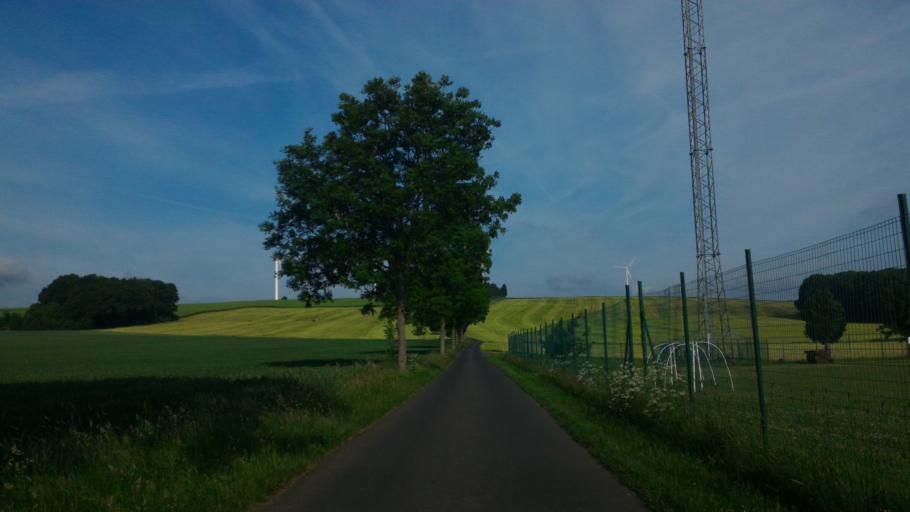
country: DE
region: Saxony
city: Leutersdorf
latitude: 50.9587
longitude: 14.6429
